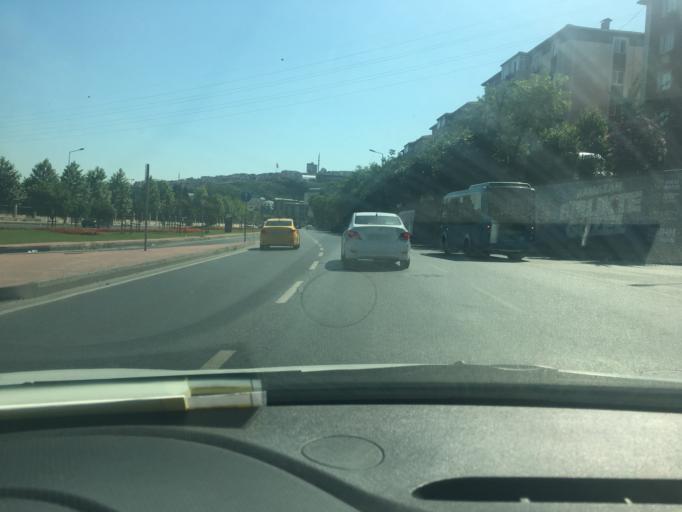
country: TR
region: Istanbul
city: Sisli
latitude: 41.0663
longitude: 28.9594
